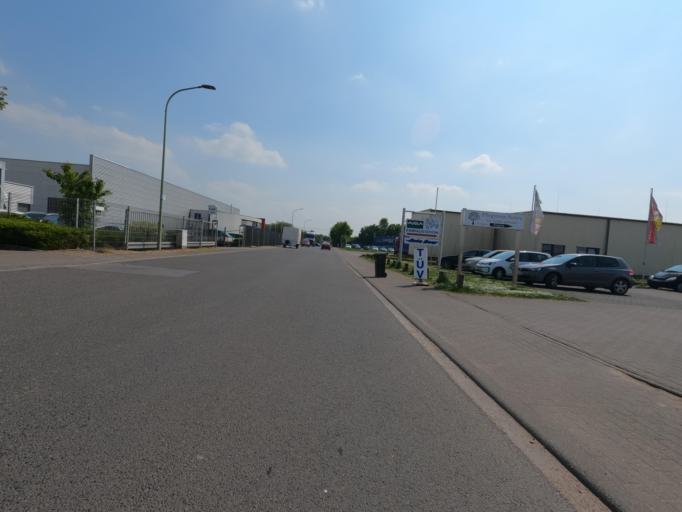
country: DE
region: North Rhine-Westphalia
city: Baesweiler
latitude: 50.9186
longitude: 6.1802
